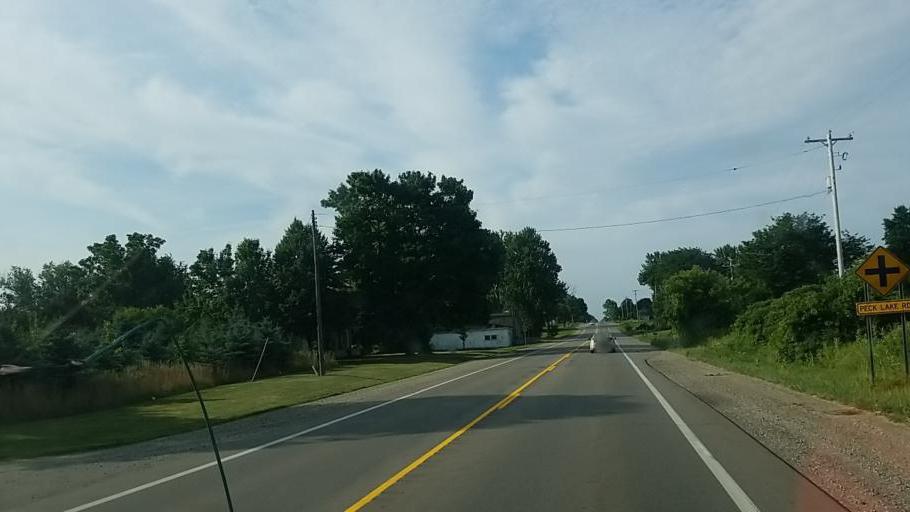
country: US
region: Michigan
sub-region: Ionia County
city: Ionia
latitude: 42.9029
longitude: -85.0749
